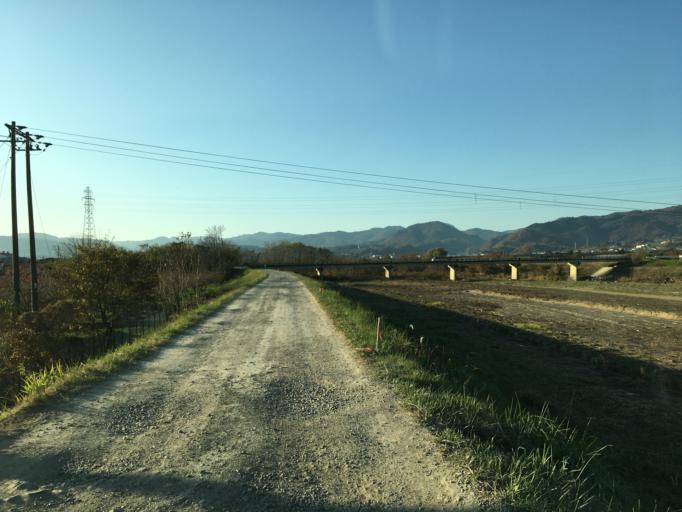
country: JP
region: Fukushima
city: Fukushima-shi
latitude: 37.8135
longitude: 140.4791
